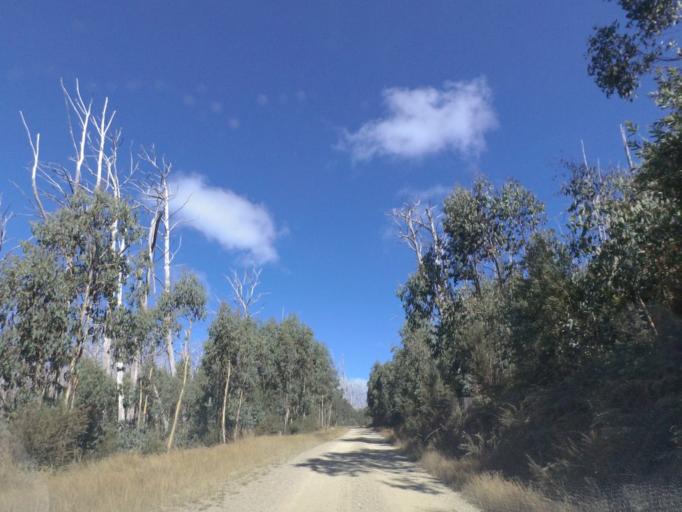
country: AU
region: Victoria
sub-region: Murrindindi
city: Alexandra
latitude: -37.4214
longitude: 145.8011
